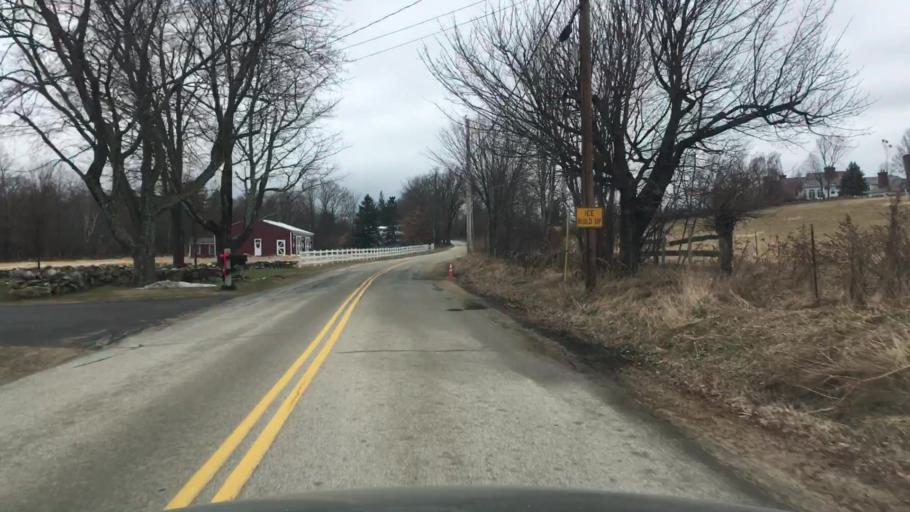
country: US
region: New Hampshire
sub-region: Hillsborough County
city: Mont Vernon
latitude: 42.9312
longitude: -71.6080
